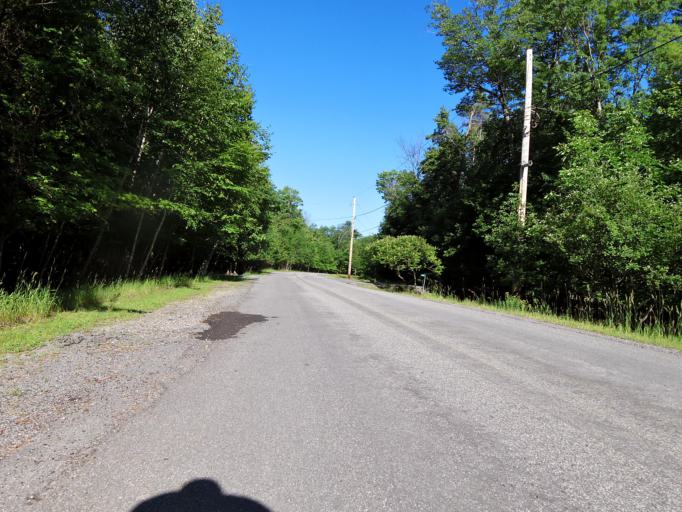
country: CA
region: Ontario
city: Arnprior
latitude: 45.4626
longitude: -76.2822
